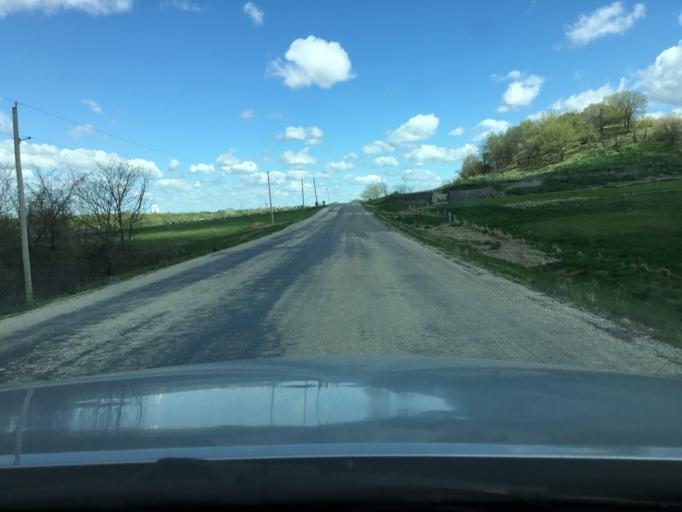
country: US
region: Kansas
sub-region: Anderson County
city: Garnett
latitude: 38.3524
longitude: -95.1253
